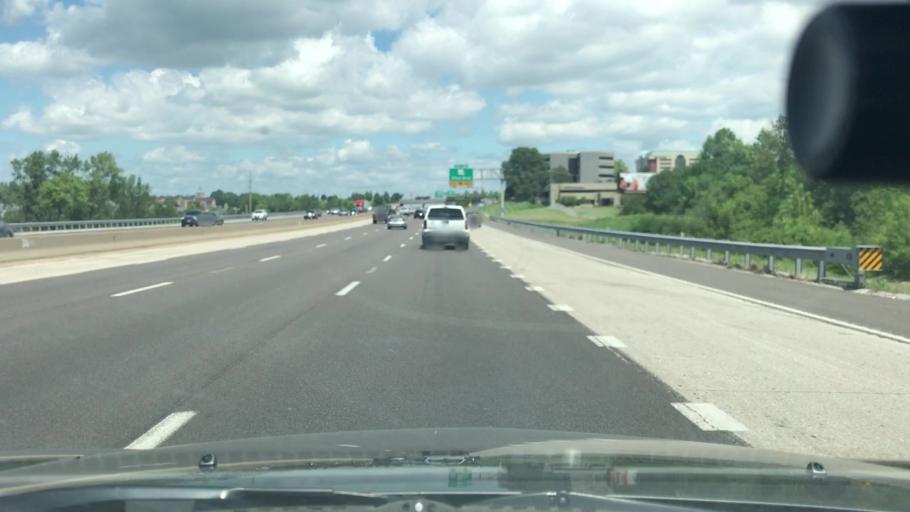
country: US
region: Missouri
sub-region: Saint Louis County
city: Creve Coeur
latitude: 38.6650
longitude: -90.4486
